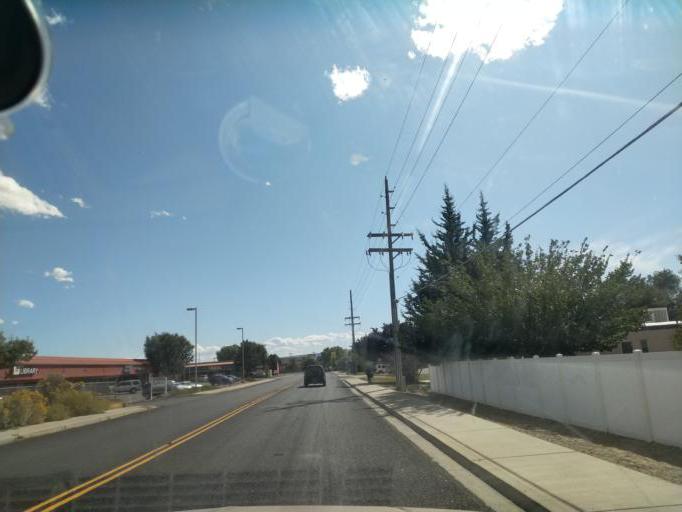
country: US
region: Colorado
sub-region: Mesa County
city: Clifton
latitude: 39.0904
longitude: -108.4595
